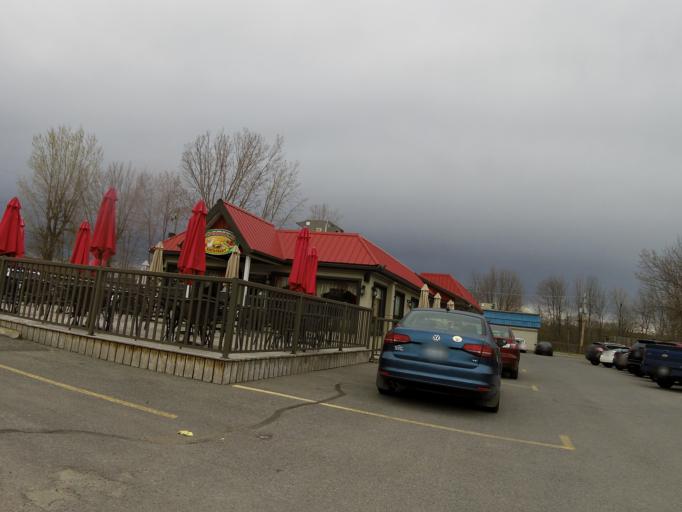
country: CA
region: Ontario
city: Hawkesbury
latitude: 45.6095
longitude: -74.6139
